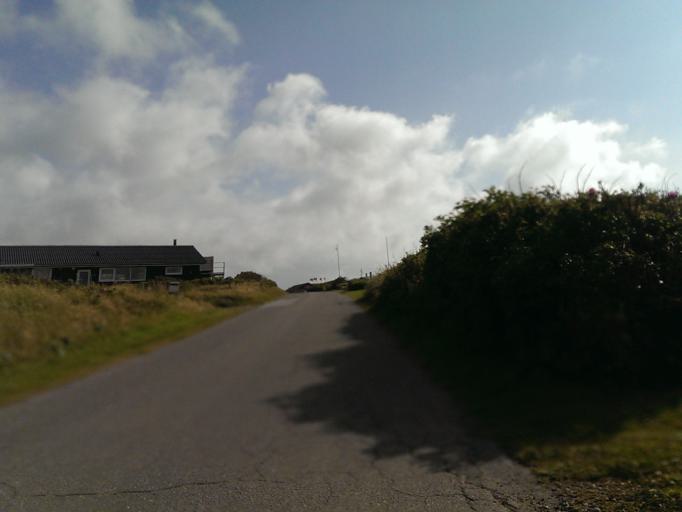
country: DK
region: North Denmark
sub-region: Jammerbugt Kommune
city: Pandrup
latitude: 57.3872
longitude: 9.7271
